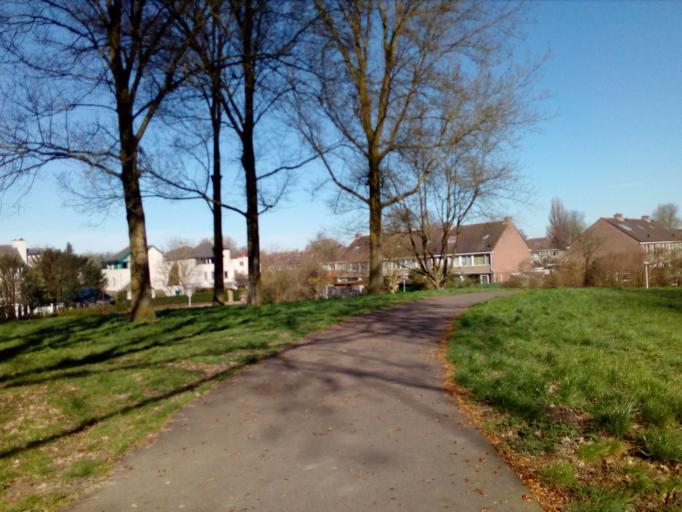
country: NL
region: South Holland
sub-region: Gemeente Zoetermeer
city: Zoetermeer
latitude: 52.0509
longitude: 4.4627
